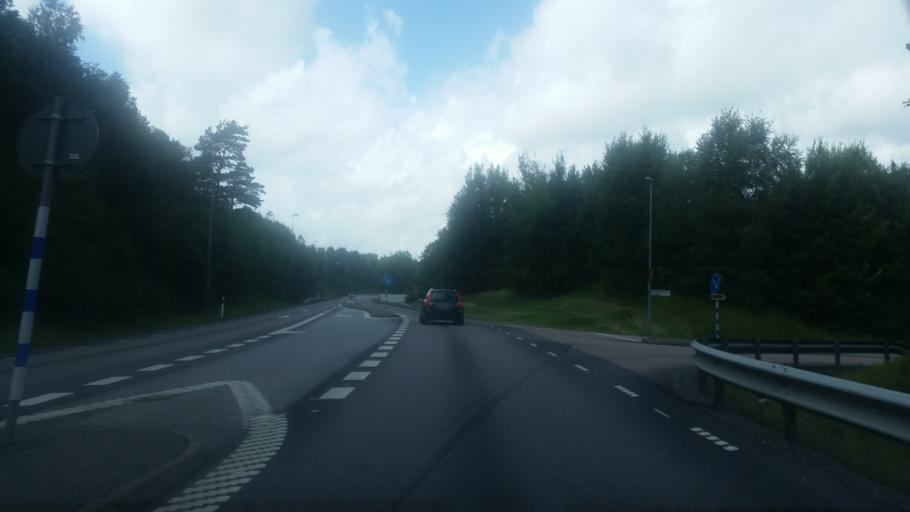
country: SE
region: Vaestra Goetaland
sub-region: Partille Kommun
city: Furulund
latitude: 57.7220
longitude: 12.1360
